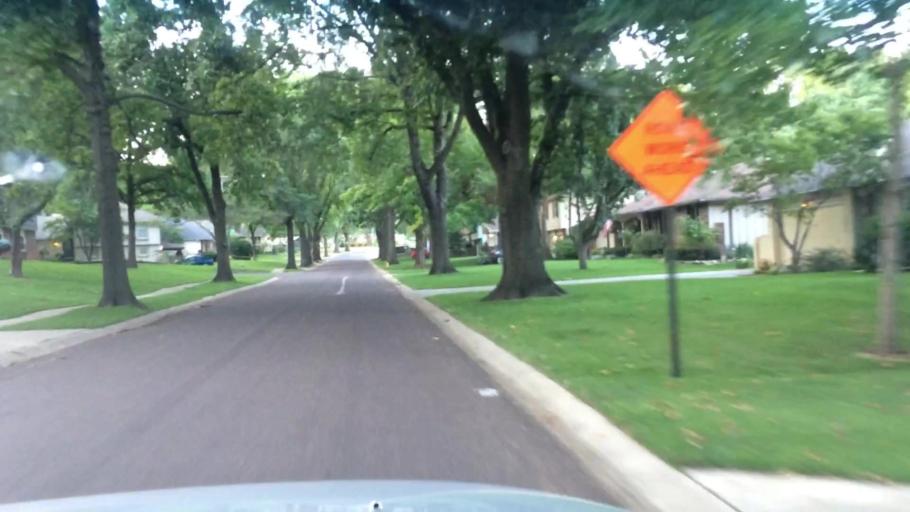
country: US
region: Kansas
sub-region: Johnson County
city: Overland Park
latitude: 38.9653
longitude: -94.6522
